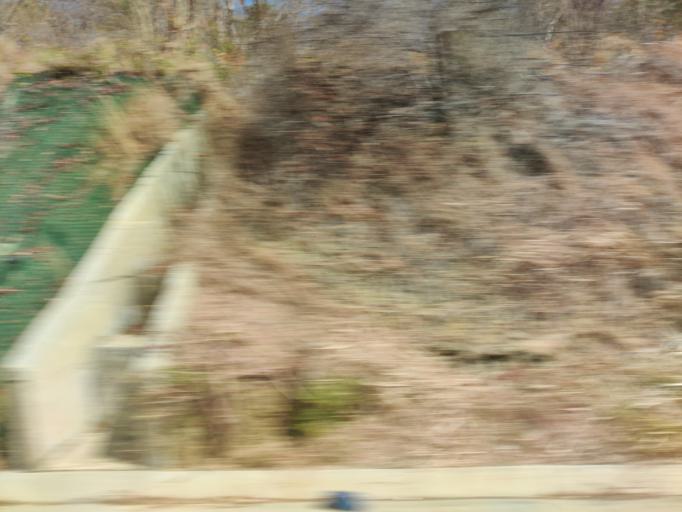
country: CO
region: Atlantico
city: Puerto Colombia
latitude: 10.9424
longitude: -75.0141
